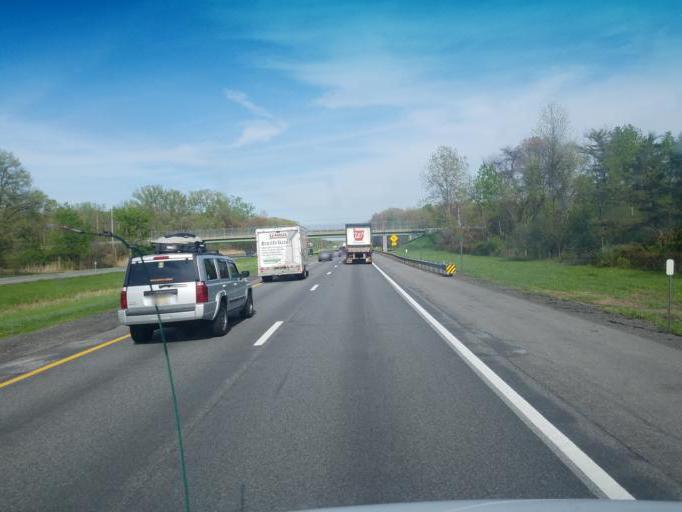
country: US
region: New York
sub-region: Madison County
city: Bolivar
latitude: 43.0952
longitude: -75.8742
